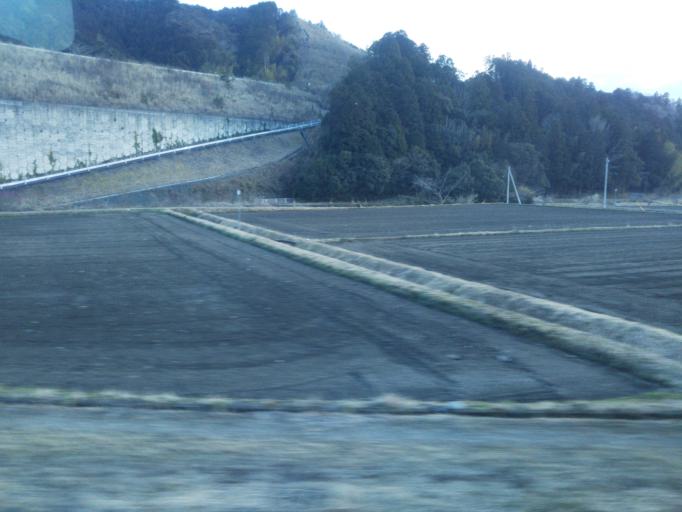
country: JP
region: Kochi
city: Susaki
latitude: 33.2770
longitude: 133.1802
